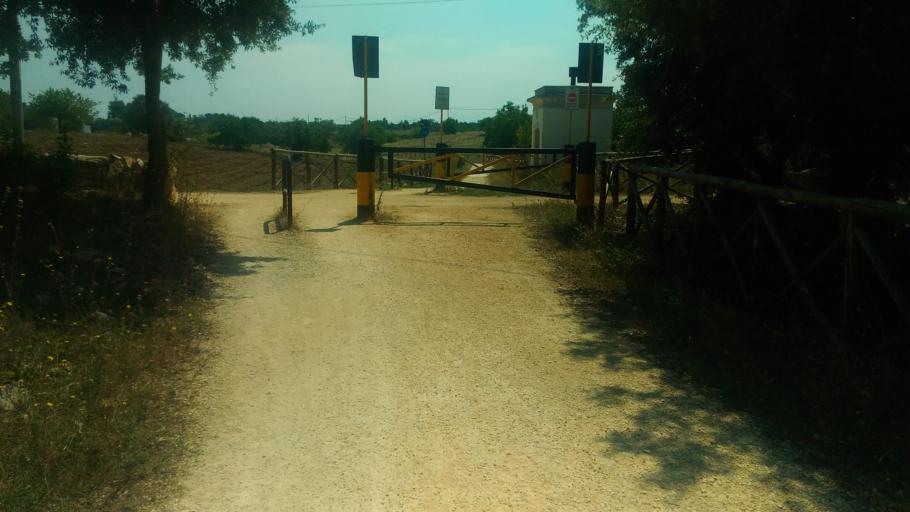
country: IT
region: Apulia
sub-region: Provincia di Brindisi
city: Cisternino
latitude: 40.7241
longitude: 17.3961
